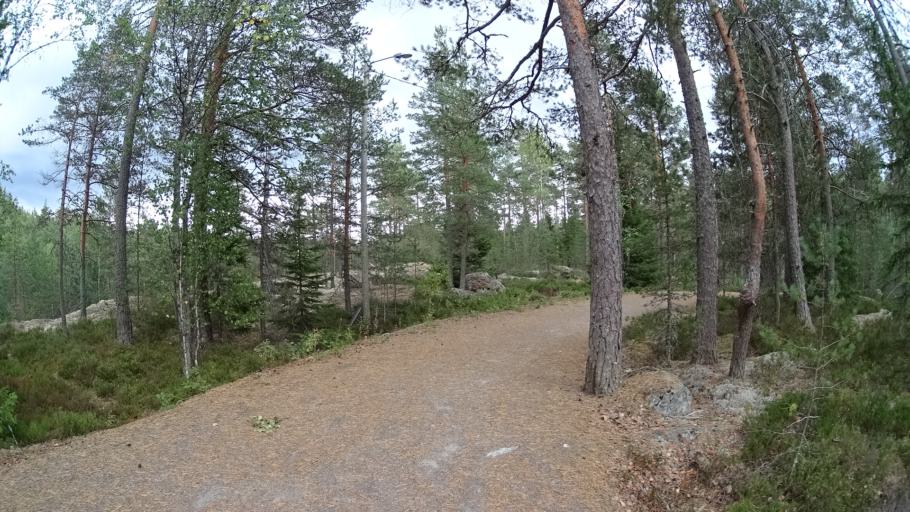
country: FI
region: Uusimaa
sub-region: Helsinki
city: Espoo
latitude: 60.2984
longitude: 24.5647
